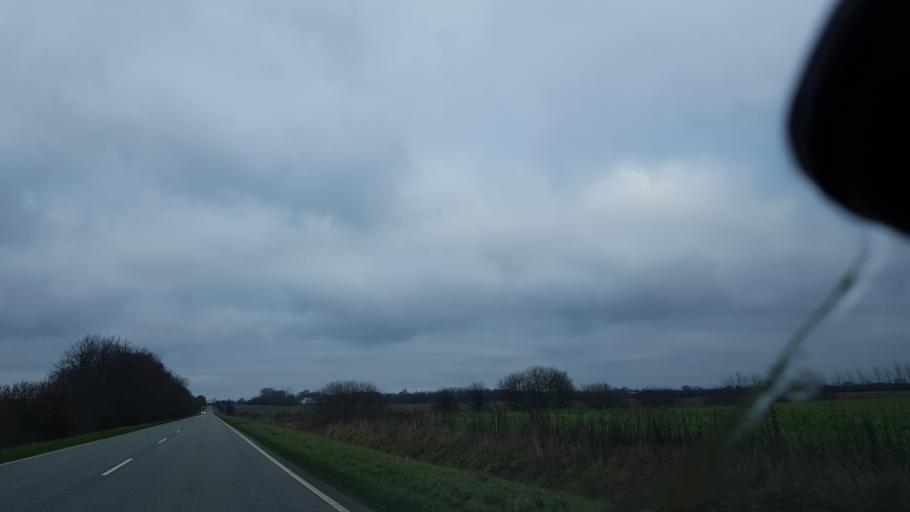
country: DK
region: South Denmark
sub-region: Haderslev Kommune
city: Vojens
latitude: 55.2338
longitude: 9.2126
